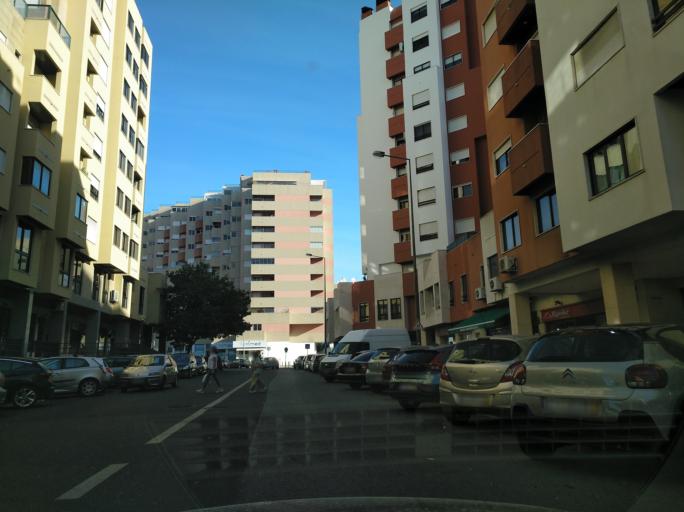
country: PT
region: Lisbon
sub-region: Odivelas
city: Pontinha
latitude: 38.7620
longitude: -9.1797
